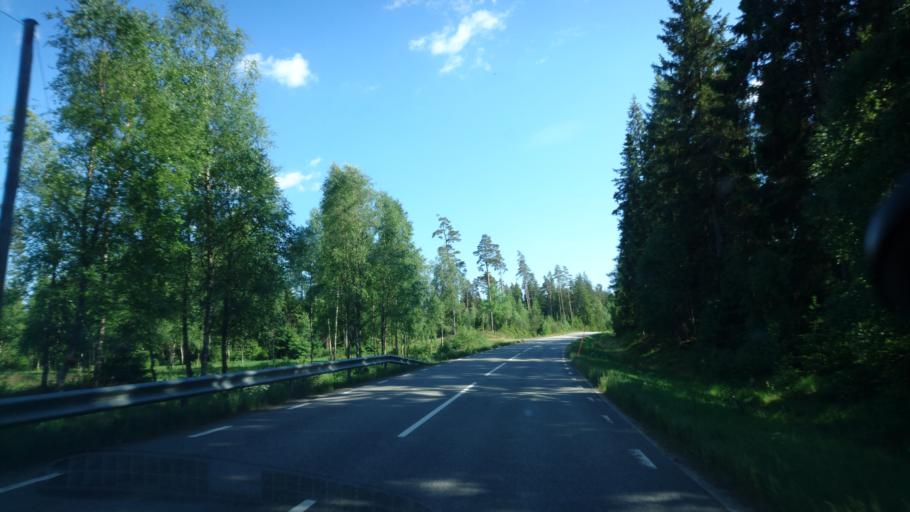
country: SE
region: Skane
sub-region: Osby Kommun
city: Lonsboda
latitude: 56.4638
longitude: 14.2330
